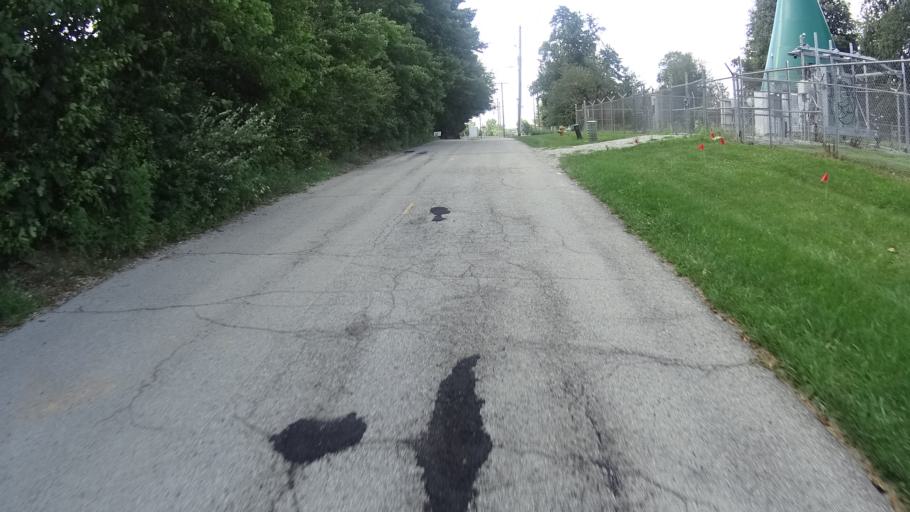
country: US
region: Indiana
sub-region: Madison County
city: Pendleton
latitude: 39.9979
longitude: -85.7384
